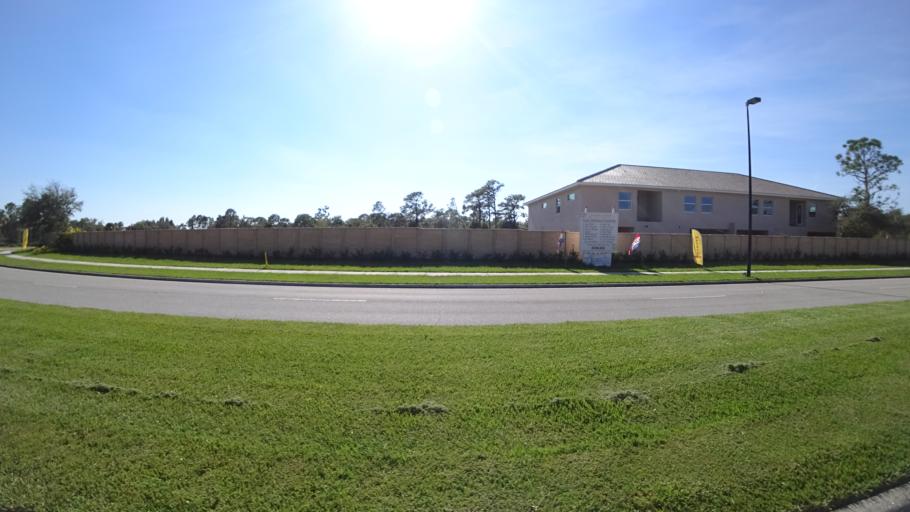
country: US
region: Florida
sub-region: Sarasota County
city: The Meadows
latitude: 27.4007
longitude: -82.4475
